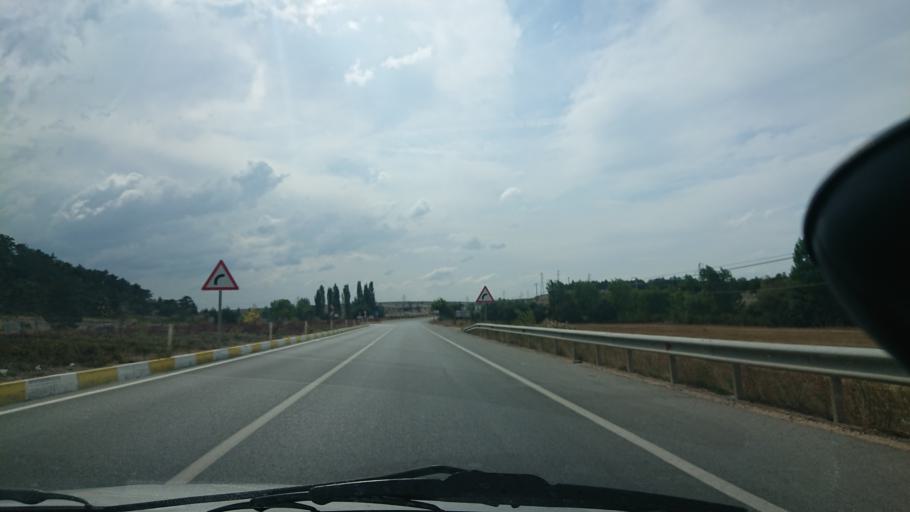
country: TR
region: Eskisehir
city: Eskisehir
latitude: 39.7264
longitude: 30.3483
